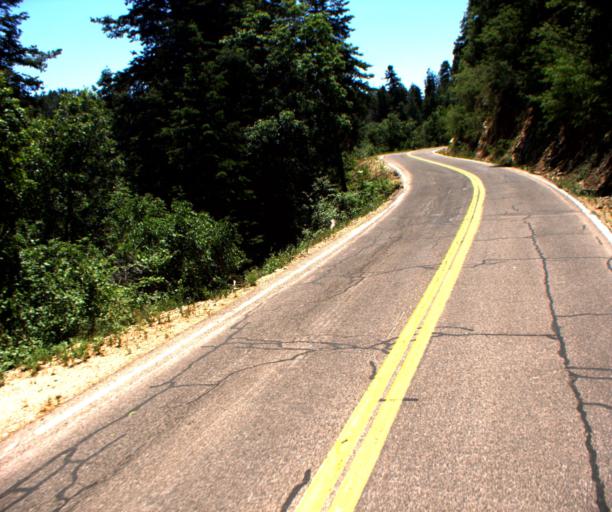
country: US
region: Arizona
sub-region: Graham County
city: Swift Trail Junction
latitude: 32.6244
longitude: -109.8269
